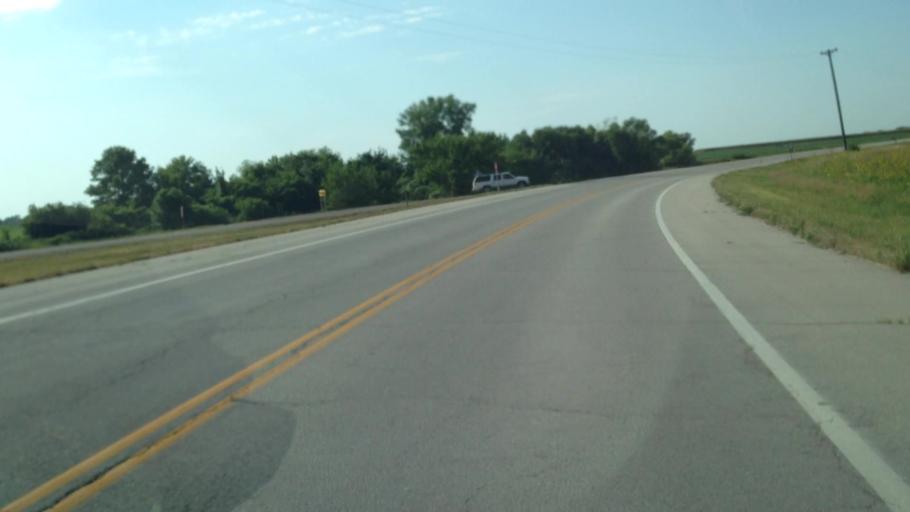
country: US
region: Kansas
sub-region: Anderson County
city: Garnett
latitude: 38.0838
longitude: -95.2425
